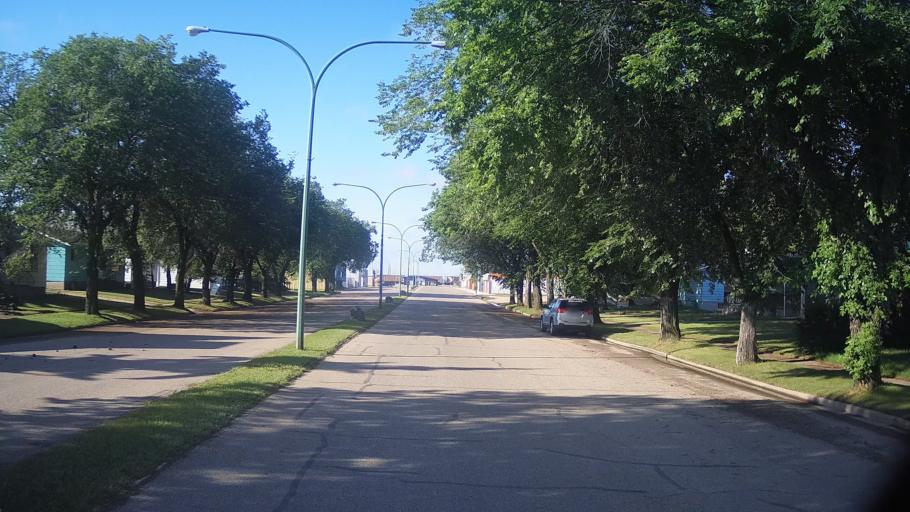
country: CA
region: Saskatchewan
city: Lanigan
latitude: 51.8483
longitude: -105.0325
